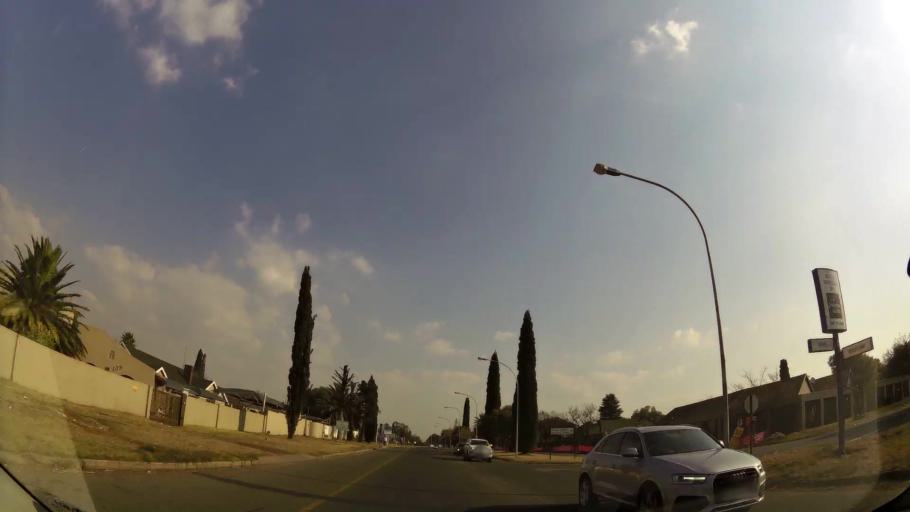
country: ZA
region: Gauteng
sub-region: Ekurhuleni Metropolitan Municipality
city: Benoni
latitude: -26.1645
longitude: 28.2815
